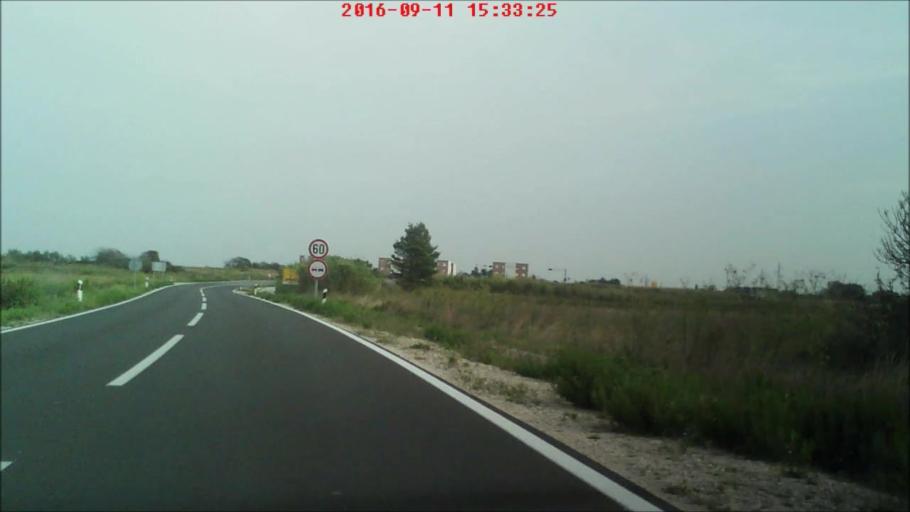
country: HR
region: Zadarska
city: Nin
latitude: 44.2476
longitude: 15.1651
